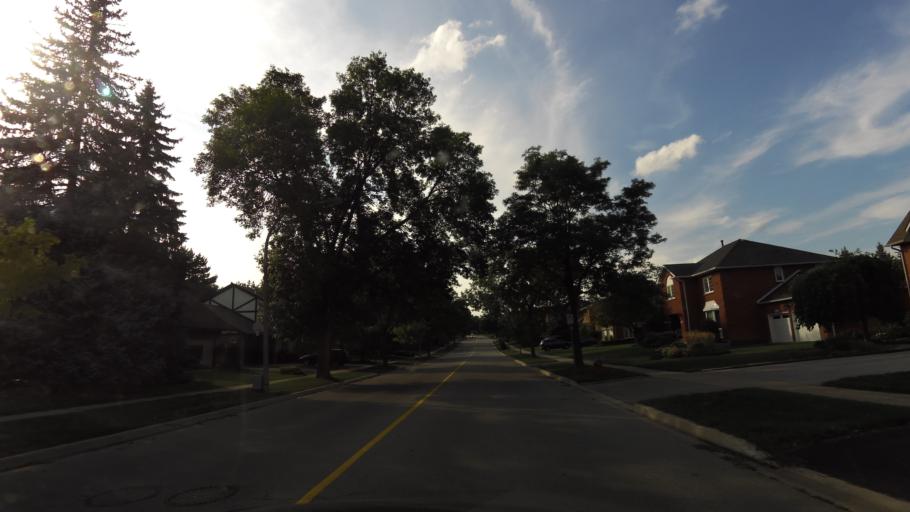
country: CA
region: Ontario
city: Burlington
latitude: 43.3418
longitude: -79.8389
